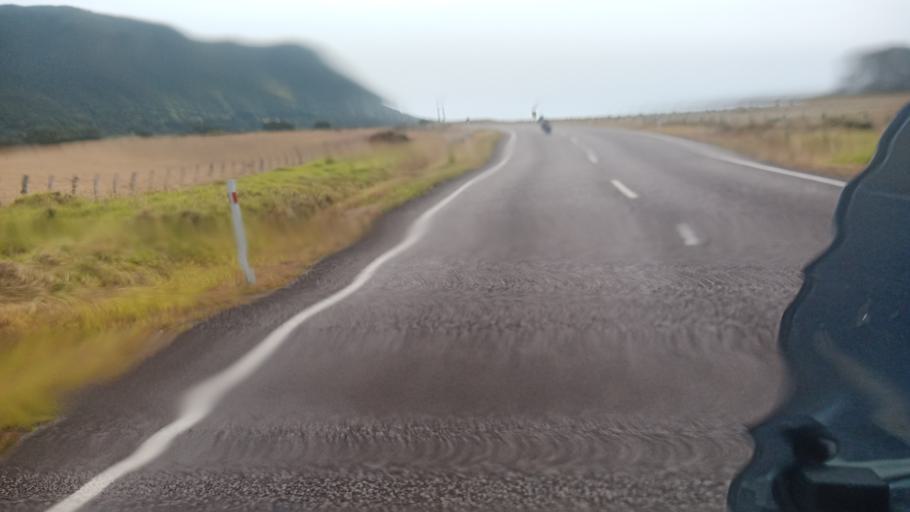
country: NZ
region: Bay of Plenty
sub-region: Opotiki District
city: Opotiki
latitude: -37.6621
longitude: 177.8508
